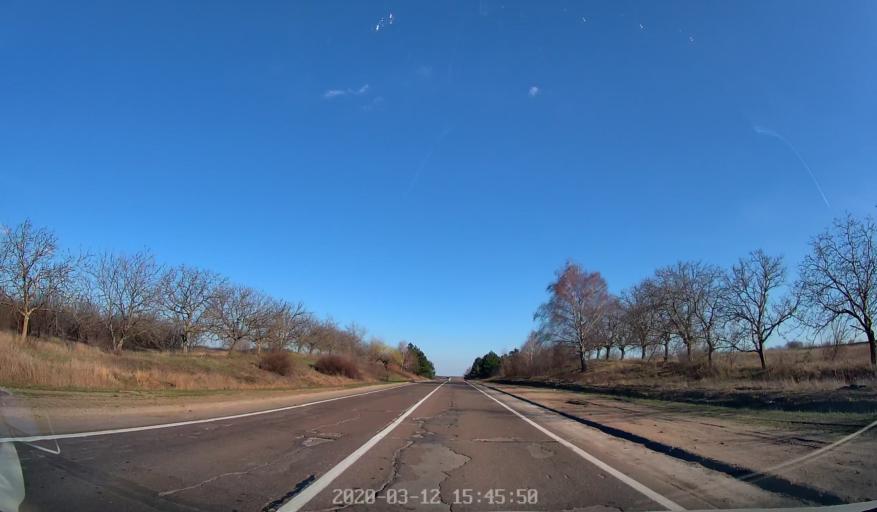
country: MD
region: Chisinau
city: Stauceni
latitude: 47.1034
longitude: 28.8821
